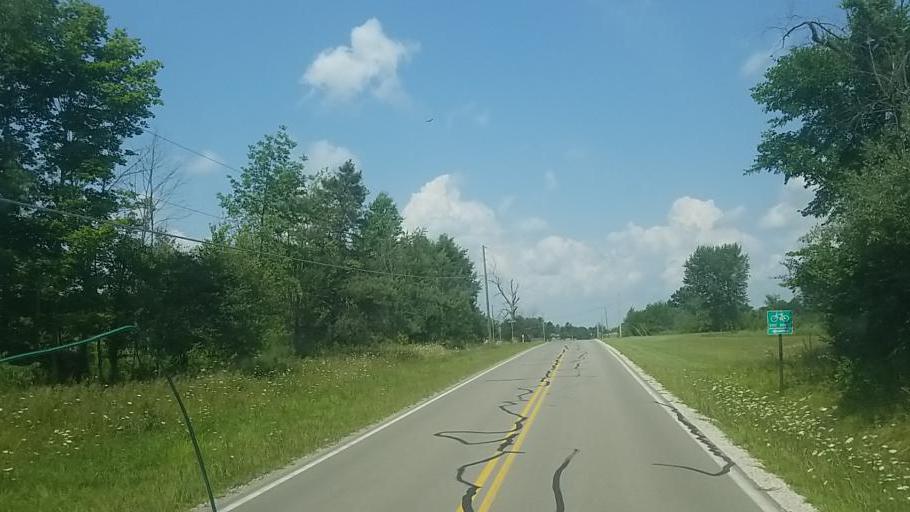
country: US
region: Ohio
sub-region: Crawford County
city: Crestline
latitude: 40.7978
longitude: -82.8004
